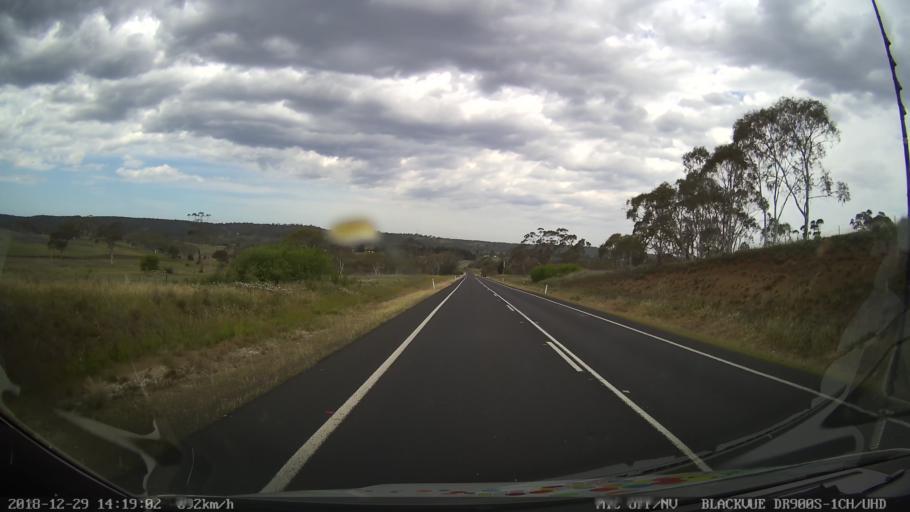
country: AU
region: New South Wales
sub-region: Cooma-Monaro
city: Cooma
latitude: -36.4949
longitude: 149.2753
